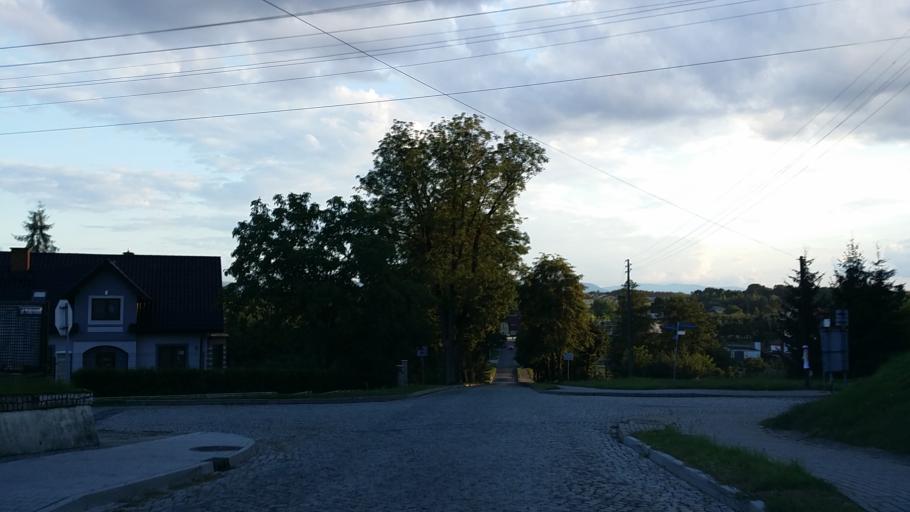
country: PL
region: Lesser Poland Voivodeship
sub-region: Powiat oswiecimski
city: Osiek
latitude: 49.9534
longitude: 19.2668
